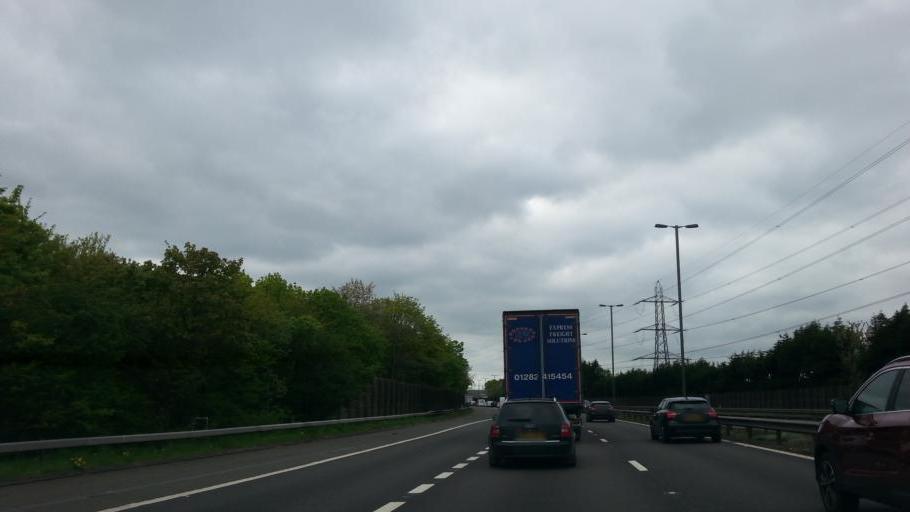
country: GB
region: England
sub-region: City and Borough of Birmingham
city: Bartley Green
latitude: 52.4556
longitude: -2.0121
